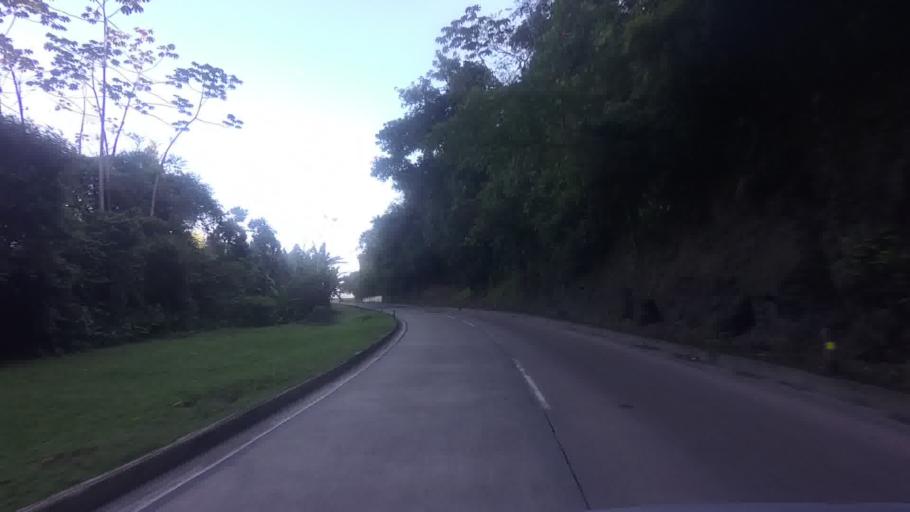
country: BR
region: Rio de Janeiro
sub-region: Petropolis
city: Petropolis
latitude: -22.5809
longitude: -43.2619
